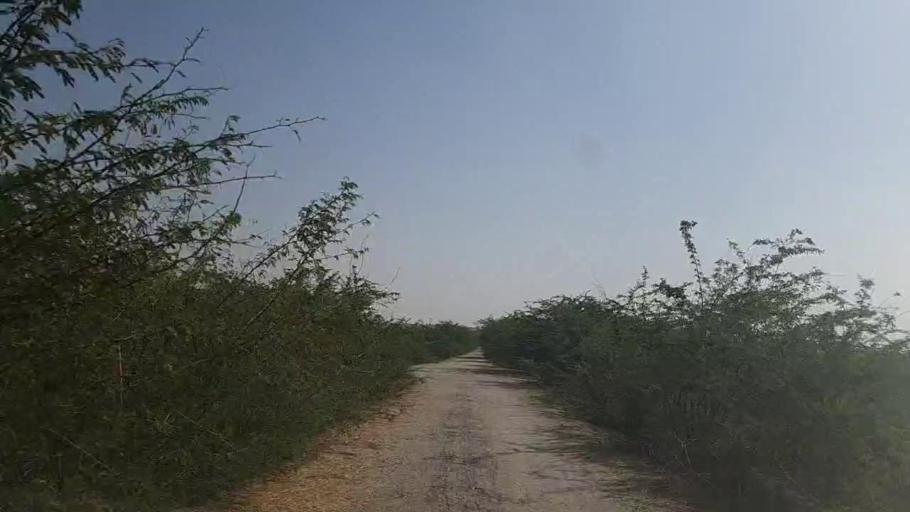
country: PK
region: Sindh
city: Naukot
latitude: 24.5794
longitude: 69.2935
